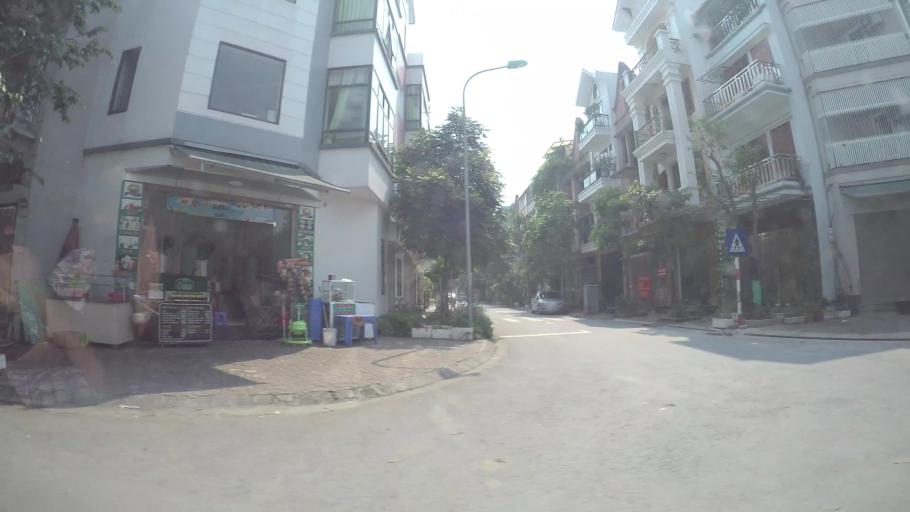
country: VN
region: Ha Noi
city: Ha Dong
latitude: 20.9724
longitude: 105.7988
